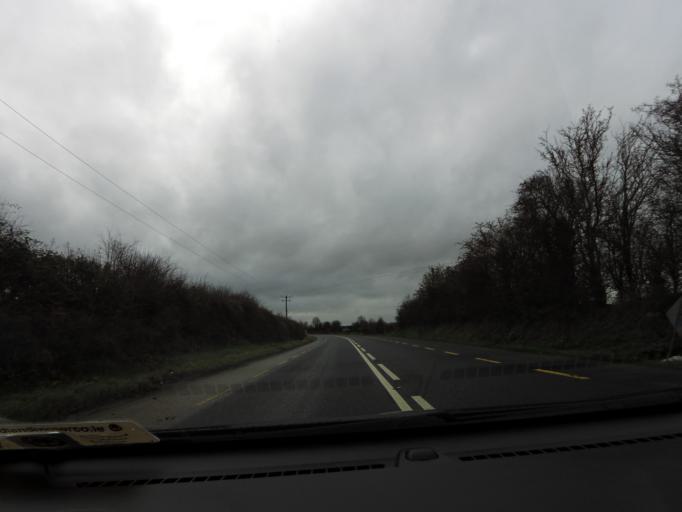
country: IE
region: Leinster
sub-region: Kilkenny
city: Ballyragget
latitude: 52.7681
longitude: -7.3325
